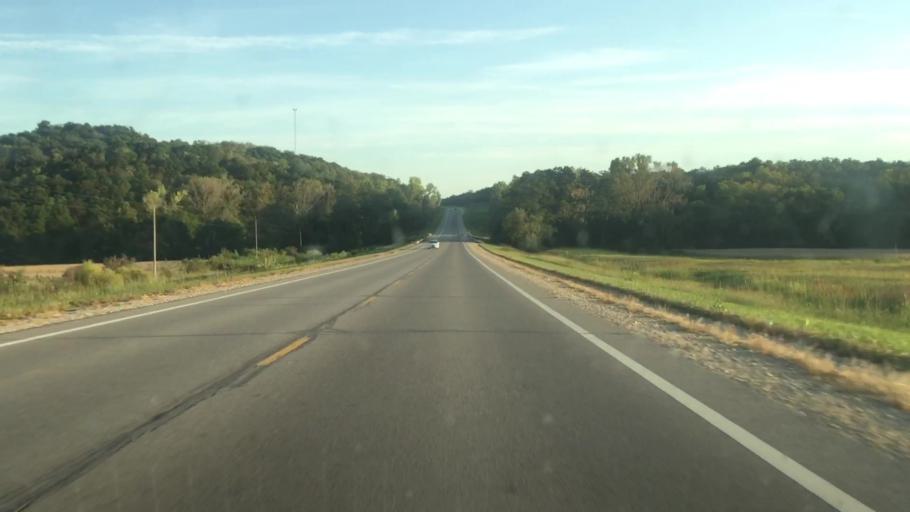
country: US
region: Kansas
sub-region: Atchison County
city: Atchison
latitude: 39.5011
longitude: -95.1325
